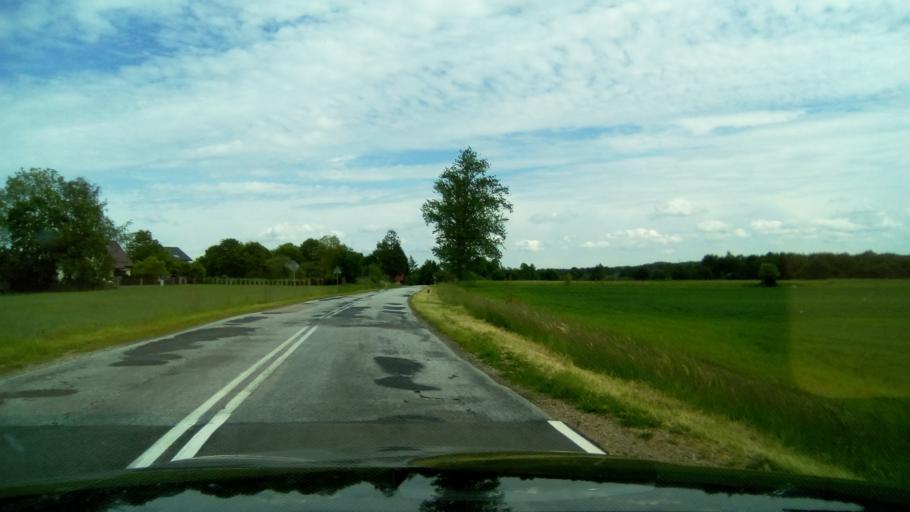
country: PL
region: Pomeranian Voivodeship
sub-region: Powiat bytowski
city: Czarna Dabrowka
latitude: 54.3321
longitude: 17.5236
